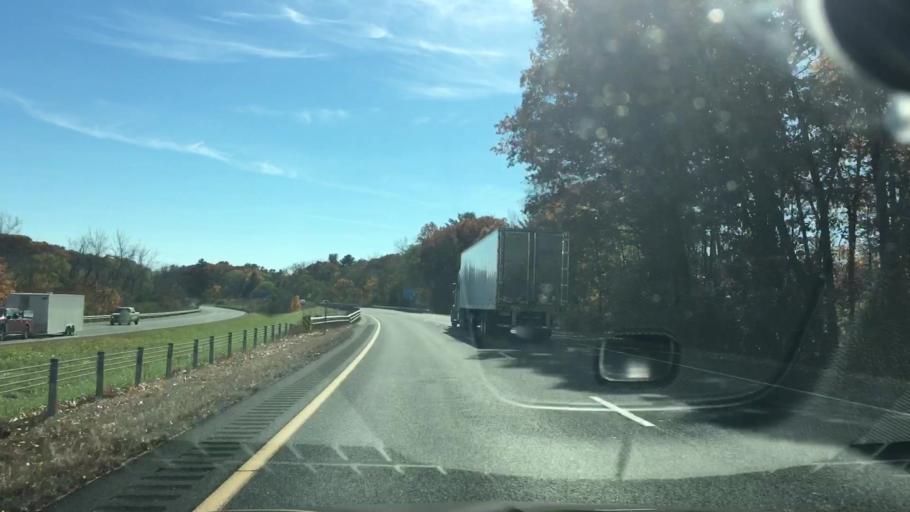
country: US
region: Massachusetts
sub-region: Hampden County
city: Holyoke
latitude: 42.2257
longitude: -72.6372
